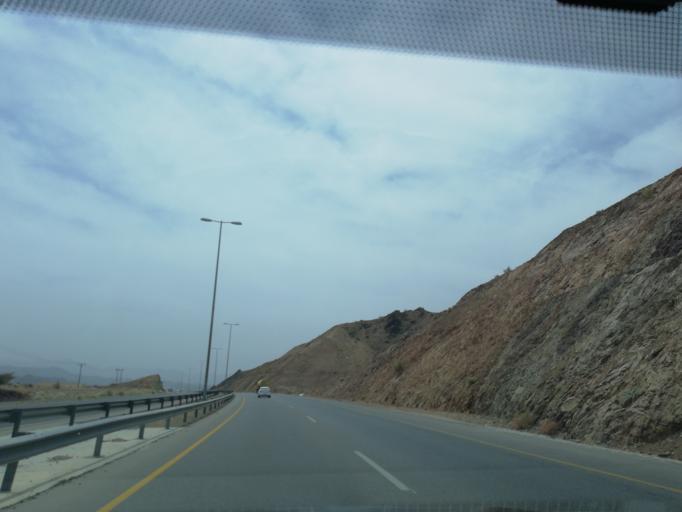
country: OM
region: Muhafazat ad Dakhiliyah
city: Sufalat Sama'il
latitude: 23.3083
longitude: 57.9427
